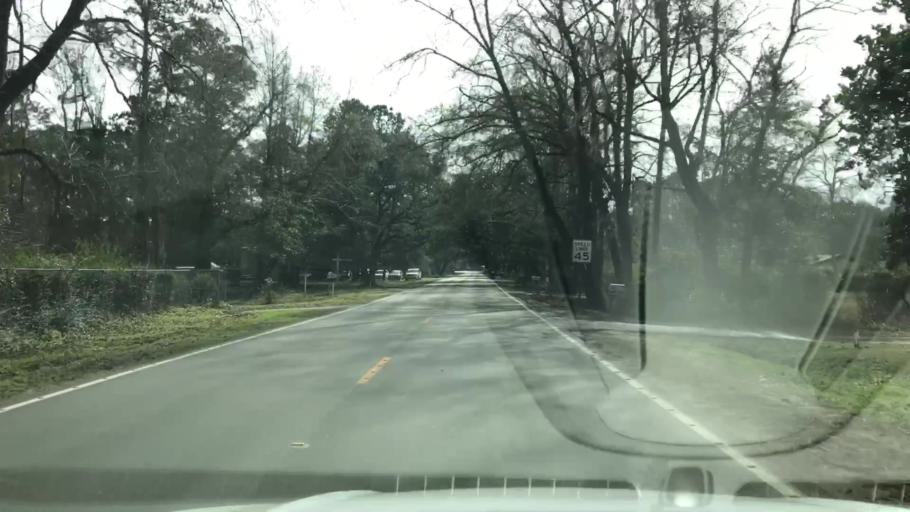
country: US
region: South Carolina
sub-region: Charleston County
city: Shell Point
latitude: 32.7359
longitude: -80.0325
